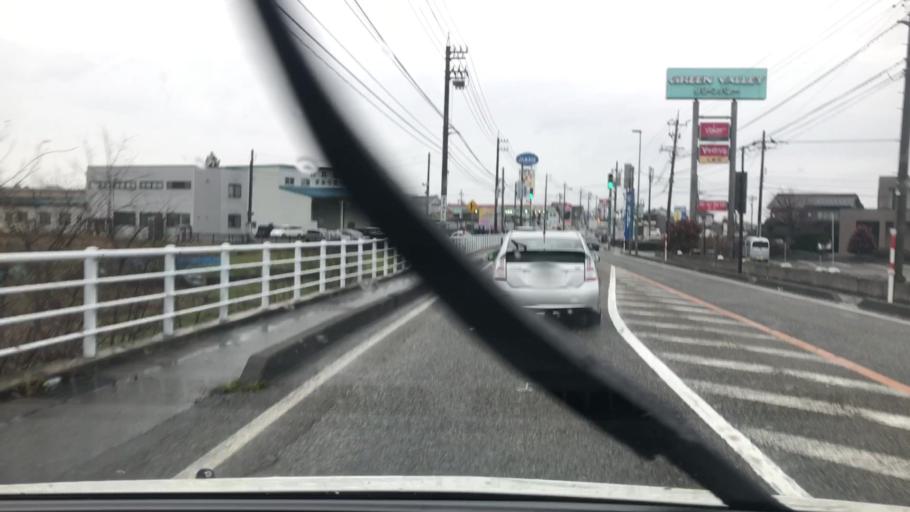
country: JP
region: Toyama
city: Yatsuomachi-higashikumisaka
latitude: 36.5933
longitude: 137.2041
